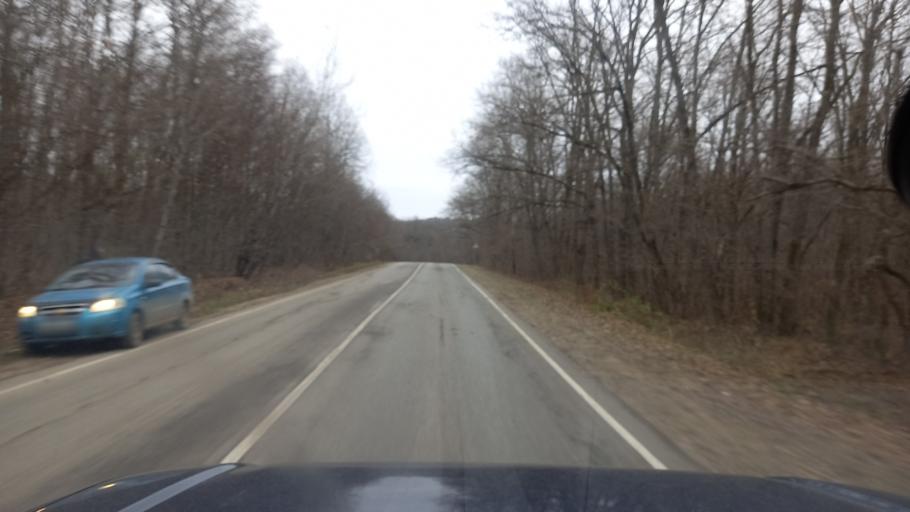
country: RU
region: Krasnodarskiy
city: Goryachiy Klyuch
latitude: 44.5441
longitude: 39.2696
